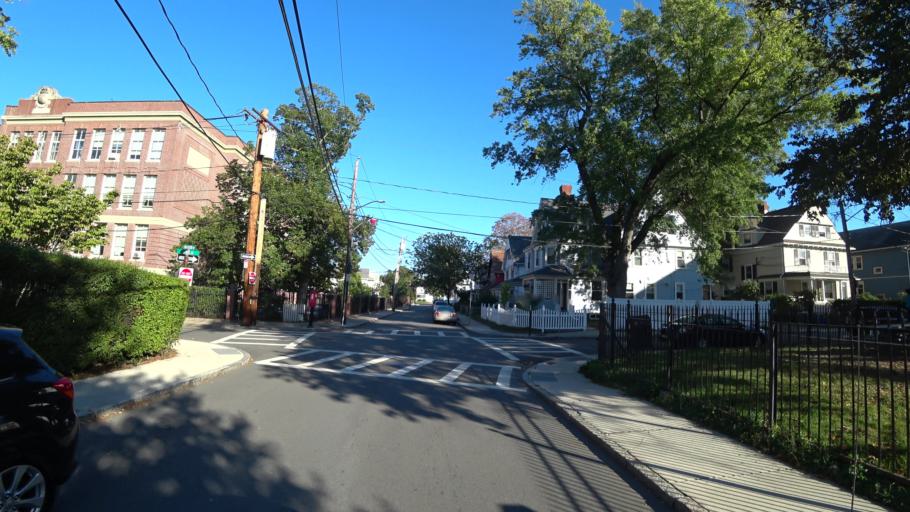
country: US
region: Massachusetts
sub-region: Norfolk County
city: Brookline
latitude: 42.3606
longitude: -71.1348
